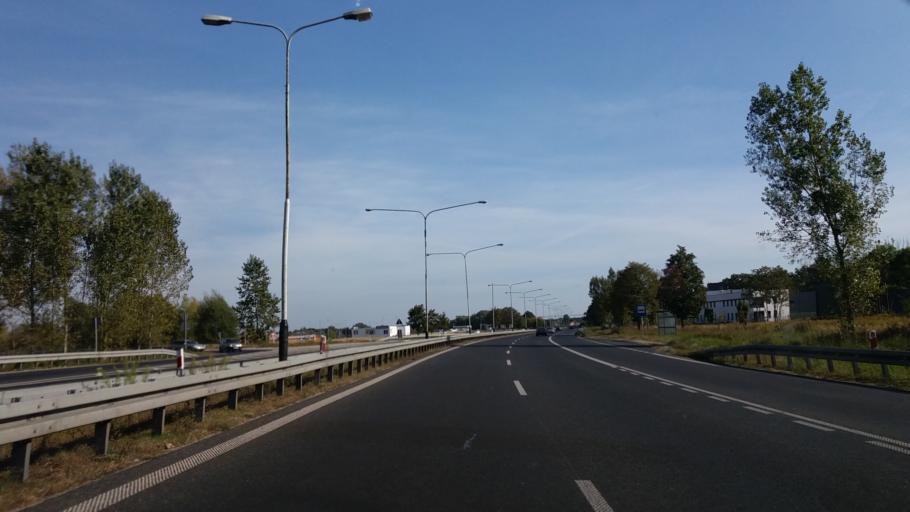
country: PL
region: Greater Poland Voivodeship
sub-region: Powiat poznanski
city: Baranowo
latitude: 52.4405
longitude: 16.7551
